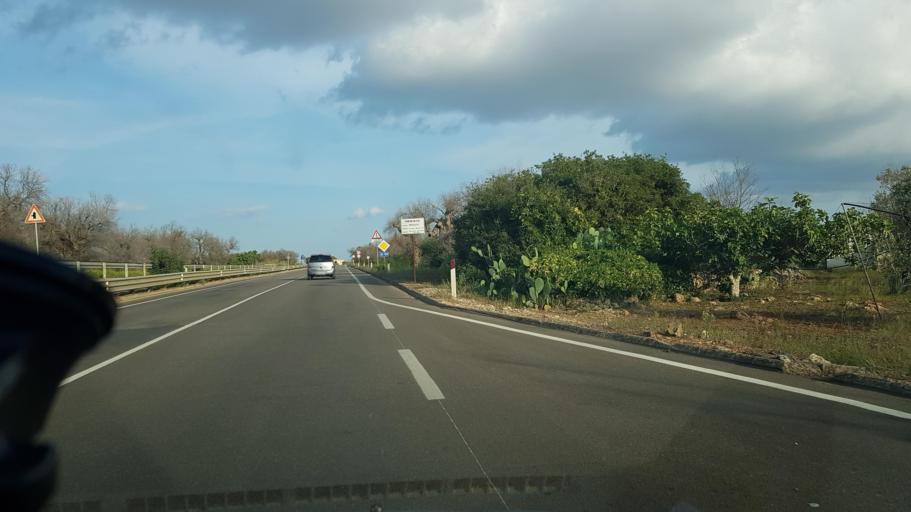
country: IT
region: Apulia
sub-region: Provincia di Lecce
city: Acquarica del Capo
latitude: 39.9175
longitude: 18.2203
